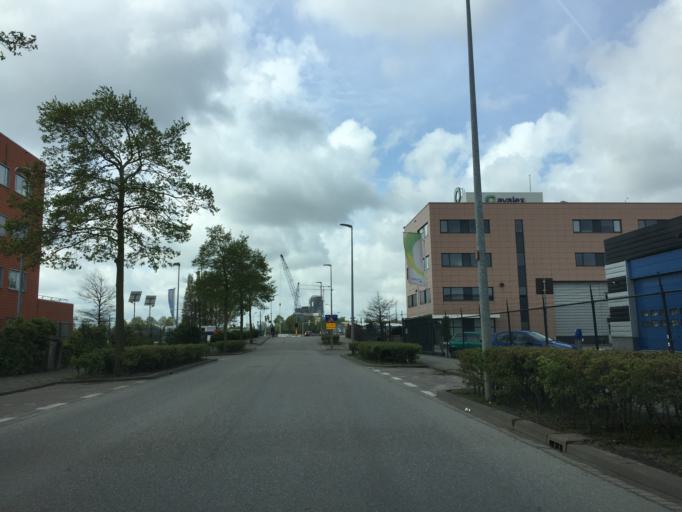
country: NL
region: South Holland
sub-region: Gemeente Den Haag
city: Ypenburg
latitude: 52.0491
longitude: 4.3559
